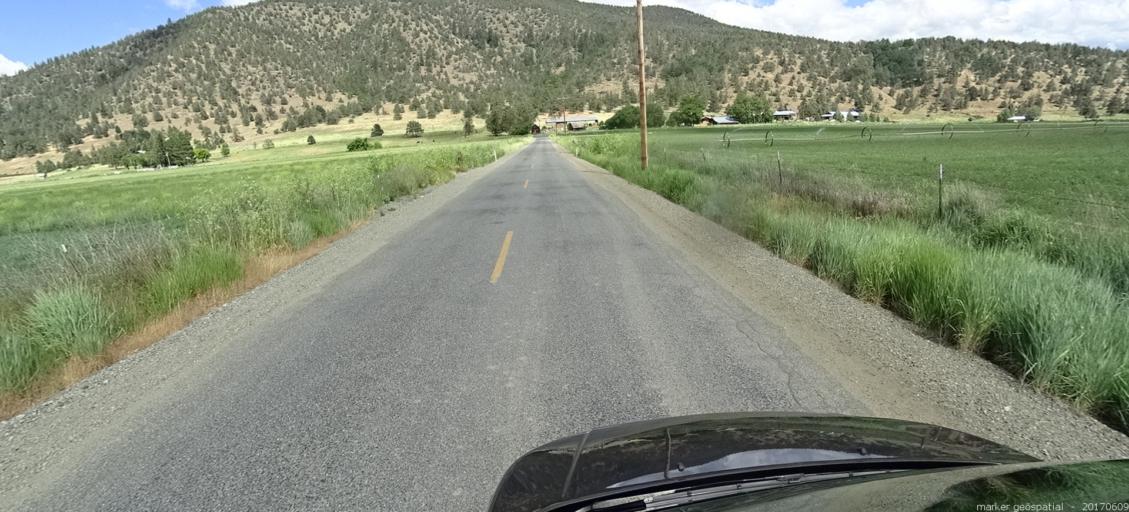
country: US
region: California
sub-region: Siskiyou County
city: Yreka
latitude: 41.5195
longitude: -122.8452
